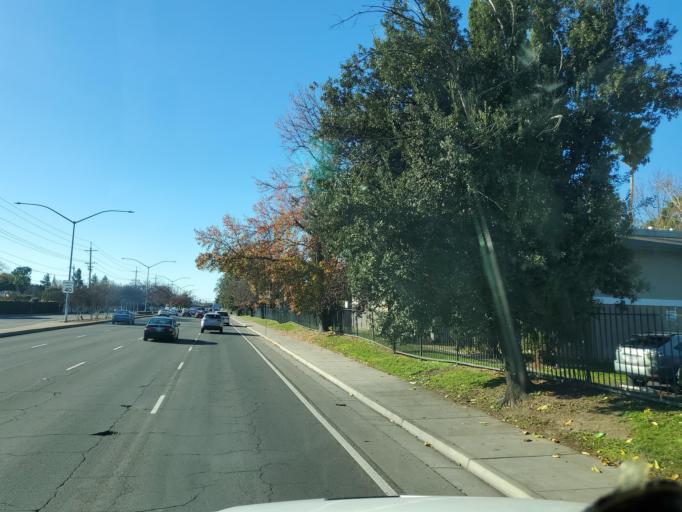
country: US
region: California
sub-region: San Joaquin County
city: Lincoln Village
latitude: 38.0209
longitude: -121.3101
